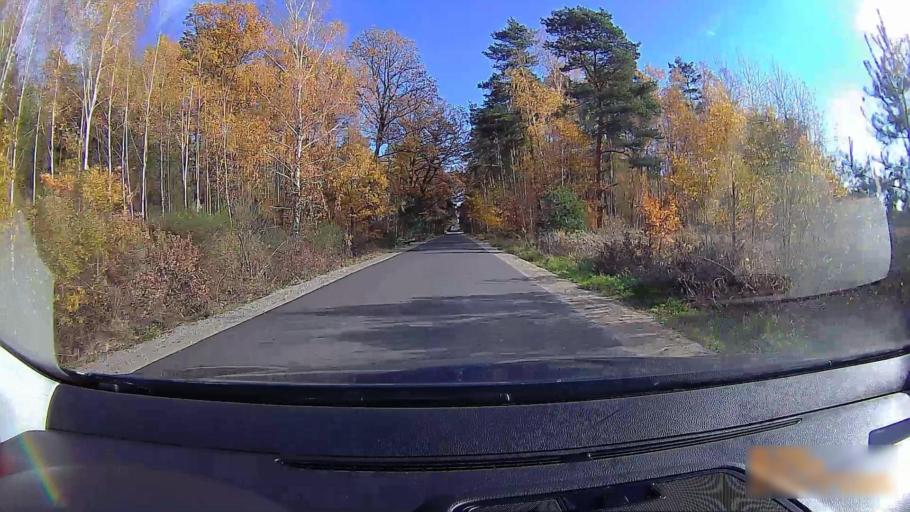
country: PL
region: Greater Poland Voivodeship
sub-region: Powiat ostrzeszowski
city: Doruchow
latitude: 51.4055
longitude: 18.0147
